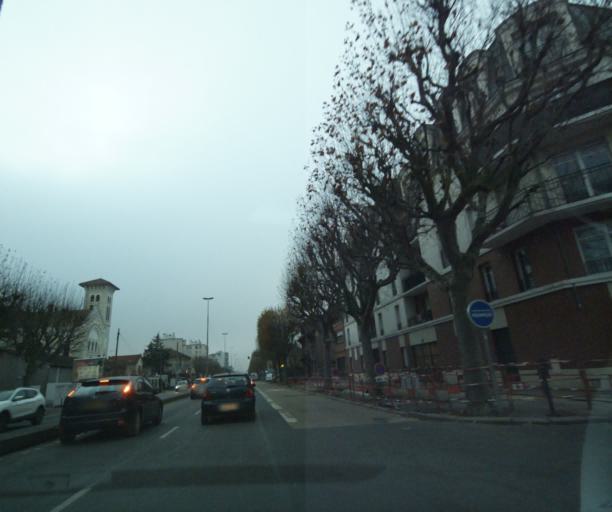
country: FR
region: Ile-de-France
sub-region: Departement de Seine-Saint-Denis
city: Les Pavillons-sous-Bois
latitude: 48.9095
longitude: 2.5050
